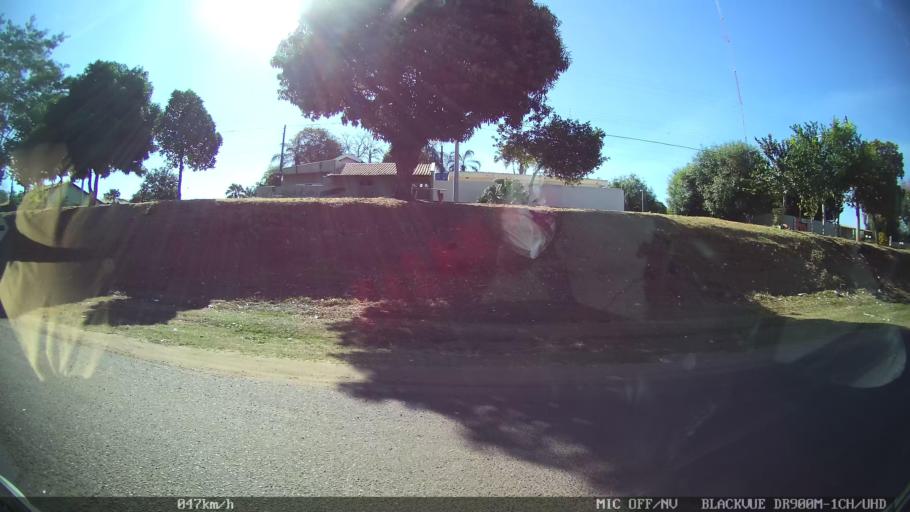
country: BR
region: Sao Paulo
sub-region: Olimpia
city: Olimpia
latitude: -20.7382
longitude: -48.8945
